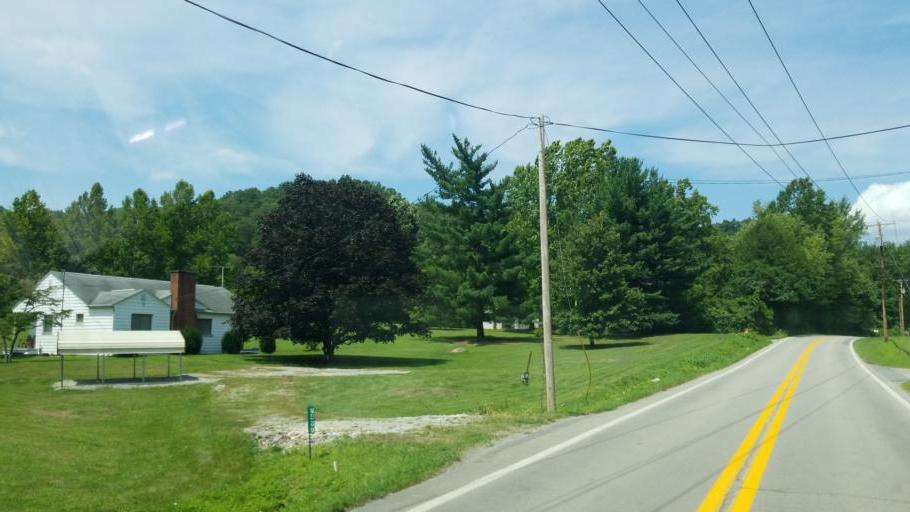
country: US
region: West Virginia
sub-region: Putnam County
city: Teays Valley
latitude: 38.4540
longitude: -81.8891
